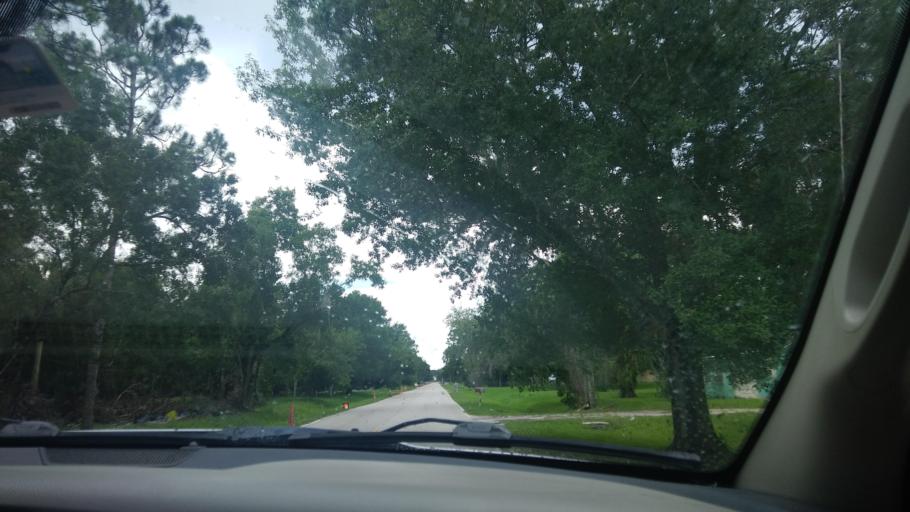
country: US
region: Florida
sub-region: Indian River County
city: Fellsmere
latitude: 27.7656
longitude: -80.6013
